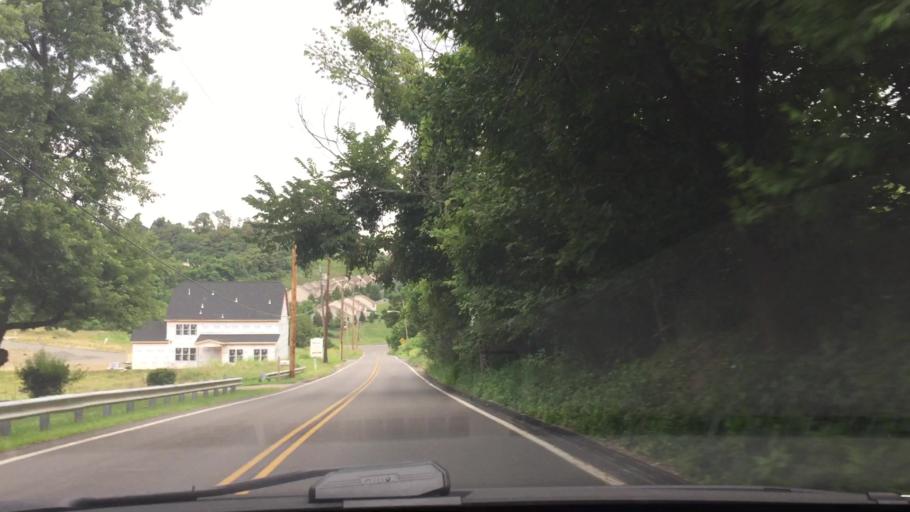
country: US
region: Pennsylvania
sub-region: Allegheny County
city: Oakdale
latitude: 40.3938
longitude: -80.1649
